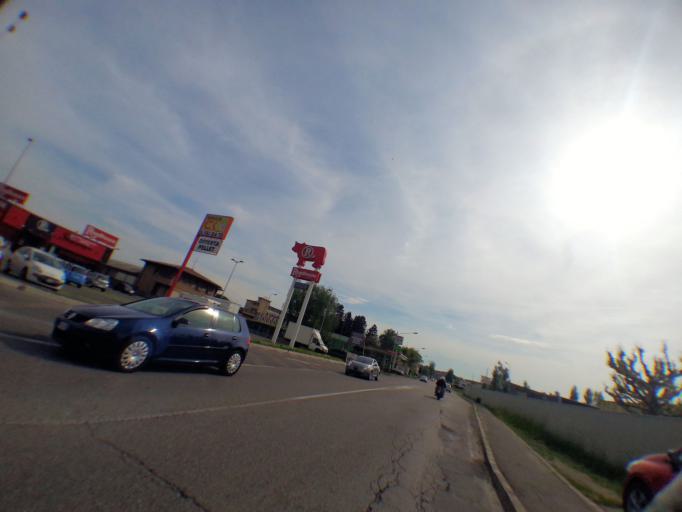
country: IT
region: Lombardy
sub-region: Provincia di Como
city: Grandate
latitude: 45.7634
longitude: 9.0560
